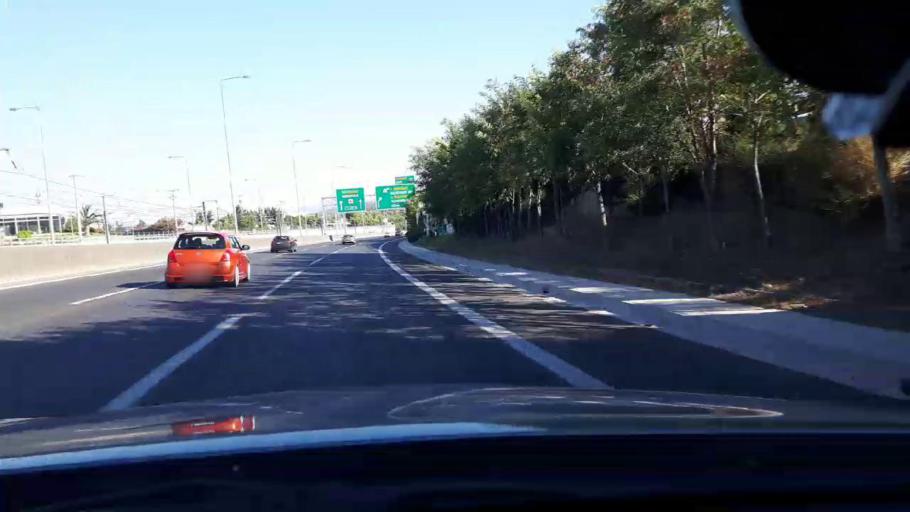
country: GR
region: Attica
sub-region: Nomarchia Anatolikis Attikis
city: Pallini
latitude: 38.0037
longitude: 23.8700
